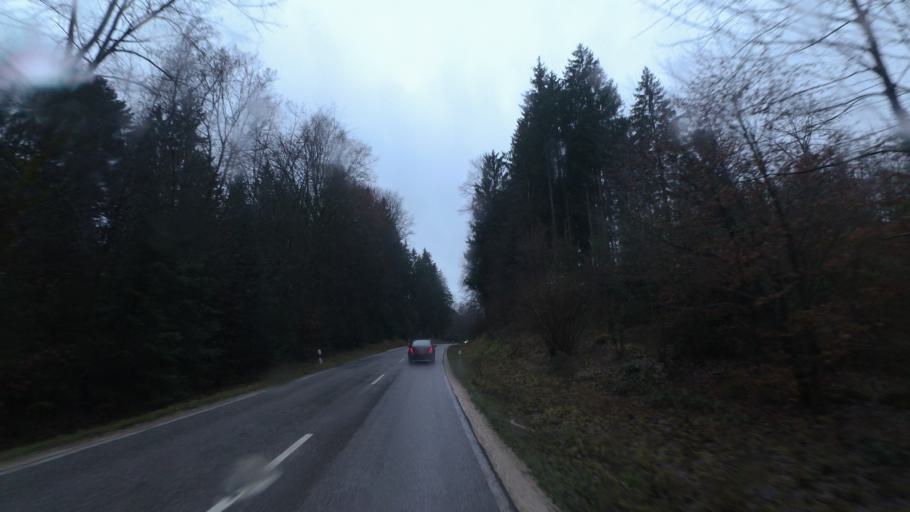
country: DE
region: Bavaria
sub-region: Upper Bavaria
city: Surberg
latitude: 47.8907
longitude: 12.6826
